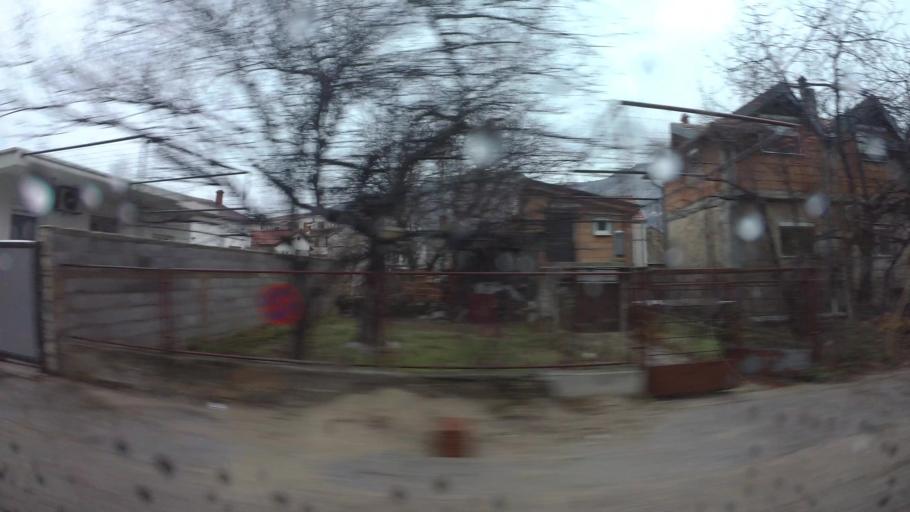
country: BA
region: Federation of Bosnia and Herzegovina
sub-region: Hercegovacko-Bosanski Kanton
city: Mostar
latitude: 43.3354
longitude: 17.8129
